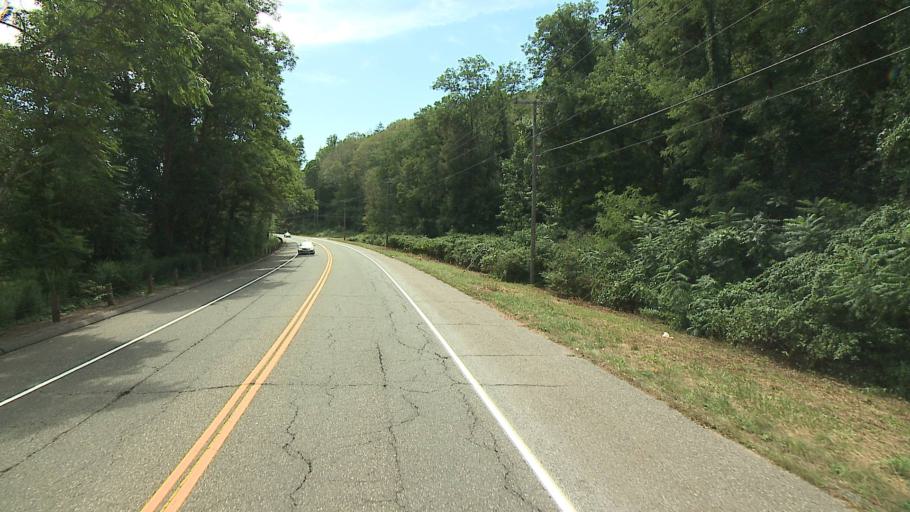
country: US
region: Connecticut
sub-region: Hartford County
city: Collinsville
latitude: 41.7886
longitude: -72.9254
